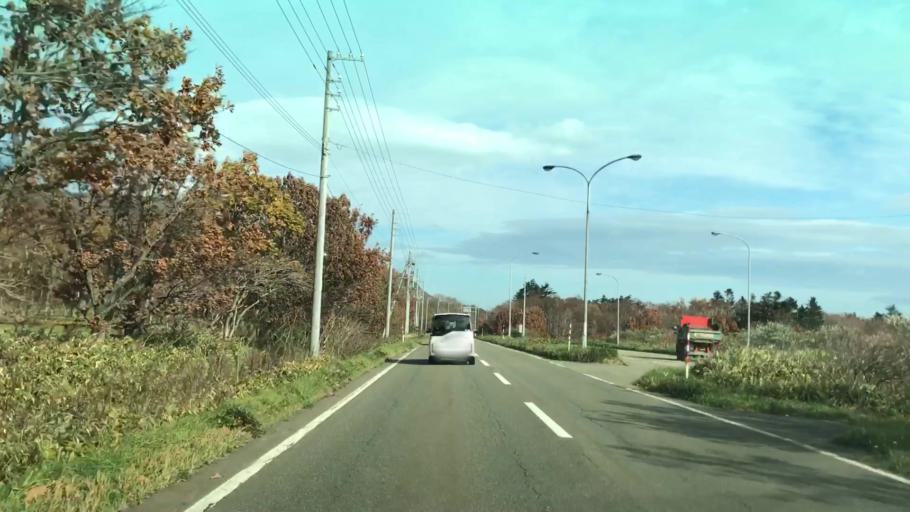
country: JP
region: Hokkaido
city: Obihiro
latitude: 42.0205
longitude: 143.2588
